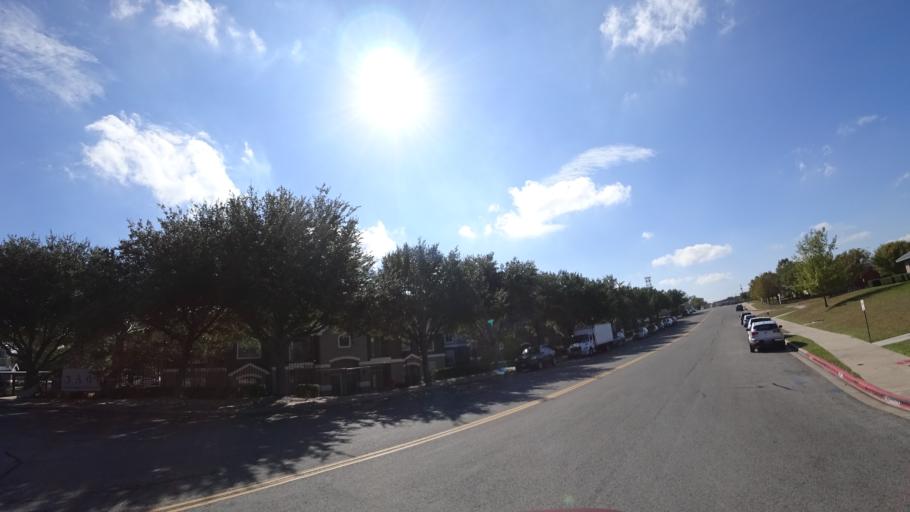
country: US
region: Texas
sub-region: Travis County
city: Windemere
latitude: 30.4492
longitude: -97.6513
